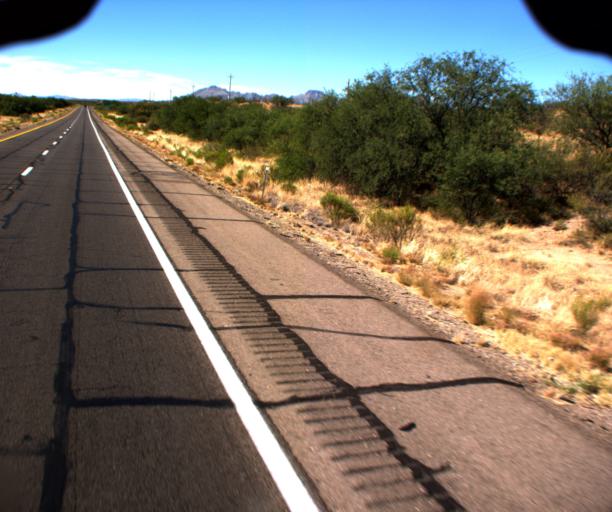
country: US
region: Arizona
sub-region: Pima County
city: Arivaca Junction
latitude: 31.6866
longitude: -111.0648
